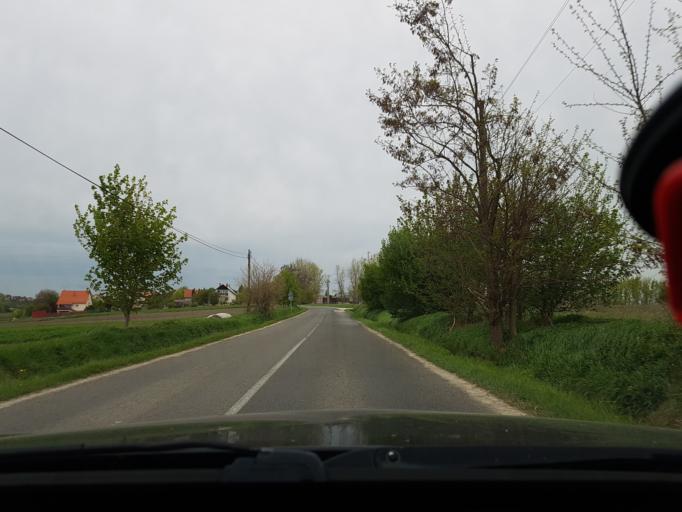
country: HU
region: Pest
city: Perbal
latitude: 47.5835
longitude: 18.7667
